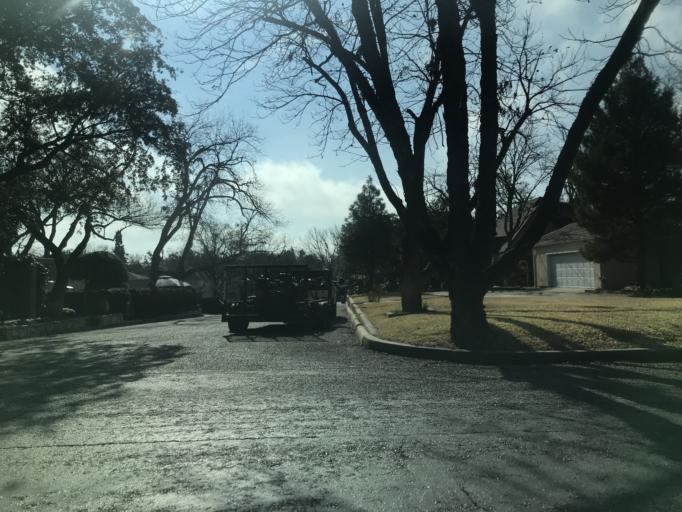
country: US
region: Texas
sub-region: Tom Green County
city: San Angelo
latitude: 31.4535
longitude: -100.4508
